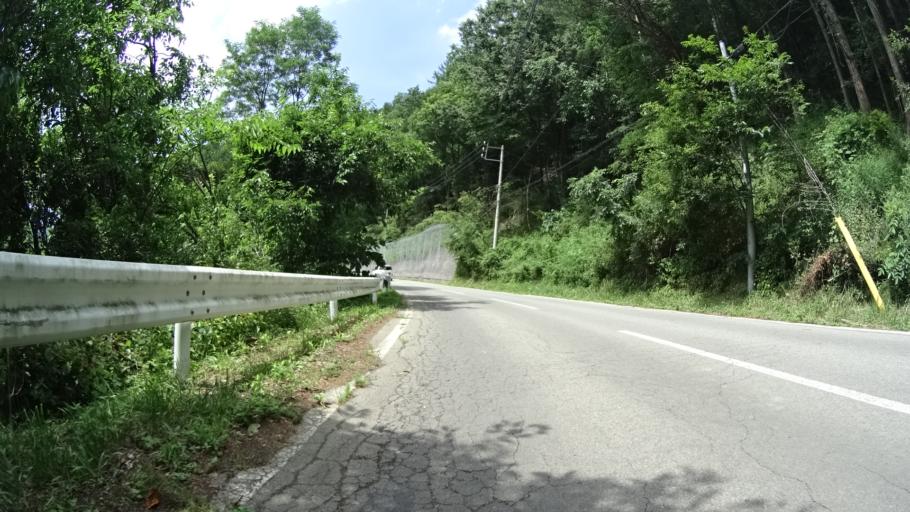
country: JP
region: Nagano
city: Saku
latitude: 36.0604
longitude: 138.5739
